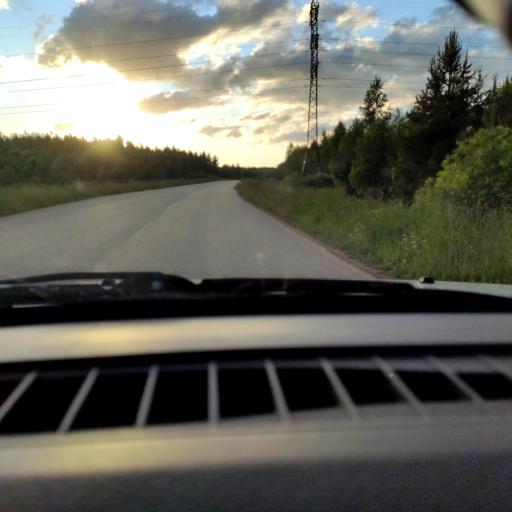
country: RU
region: Perm
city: Polazna
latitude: 58.2052
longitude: 56.4671
